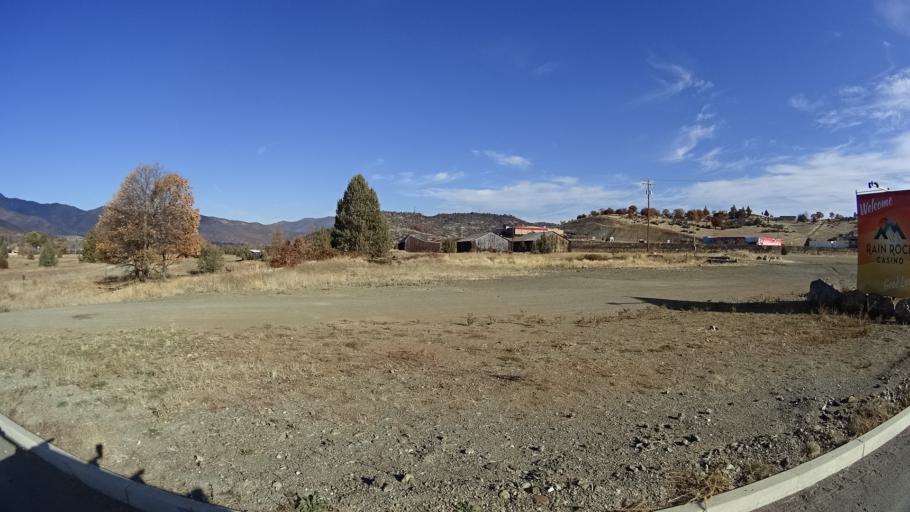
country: US
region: California
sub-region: Siskiyou County
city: Yreka
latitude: 41.7085
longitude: -122.6332
